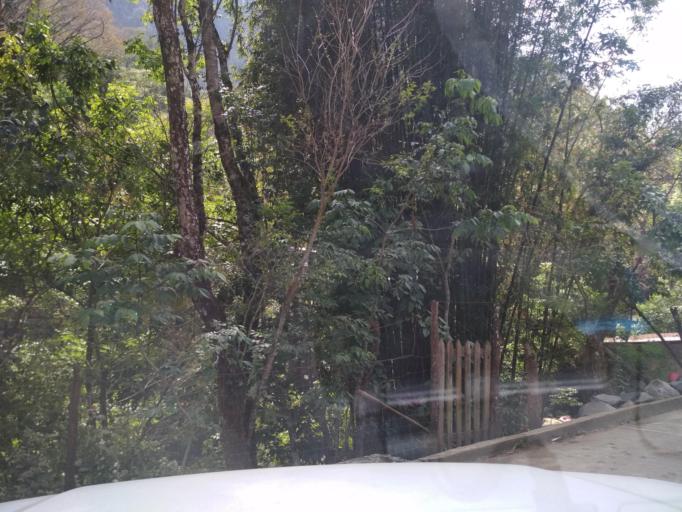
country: MX
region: Veracruz
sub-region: Tlilapan
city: Tonalixco
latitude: 18.7886
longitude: -97.0932
